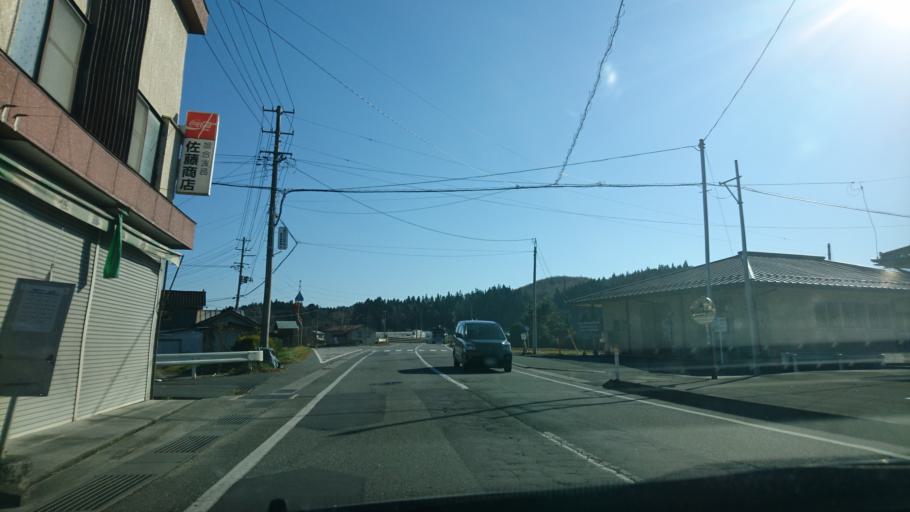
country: JP
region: Iwate
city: Ichinoseki
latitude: 38.9919
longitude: 141.2839
